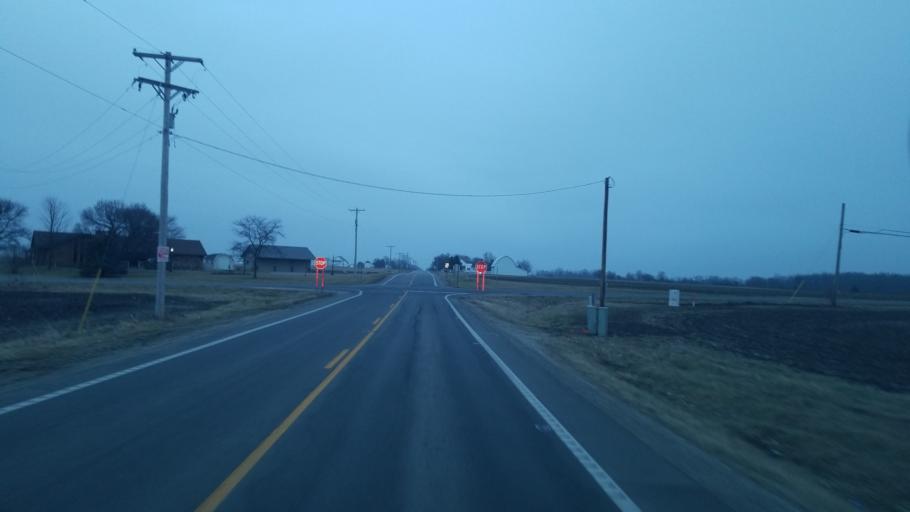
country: US
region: Ohio
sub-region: Mercer County
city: Rockford
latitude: 40.6550
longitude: -84.6486
